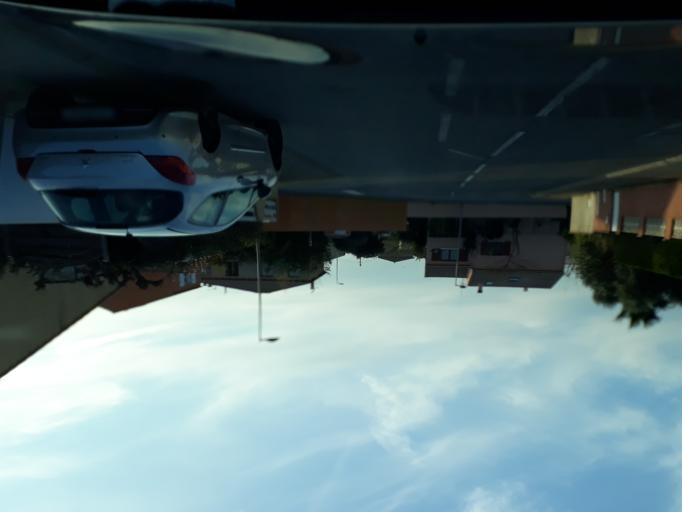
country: FR
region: Languedoc-Roussillon
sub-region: Departement de l'Herault
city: Marseillan
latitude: 43.3506
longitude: 3.5295
